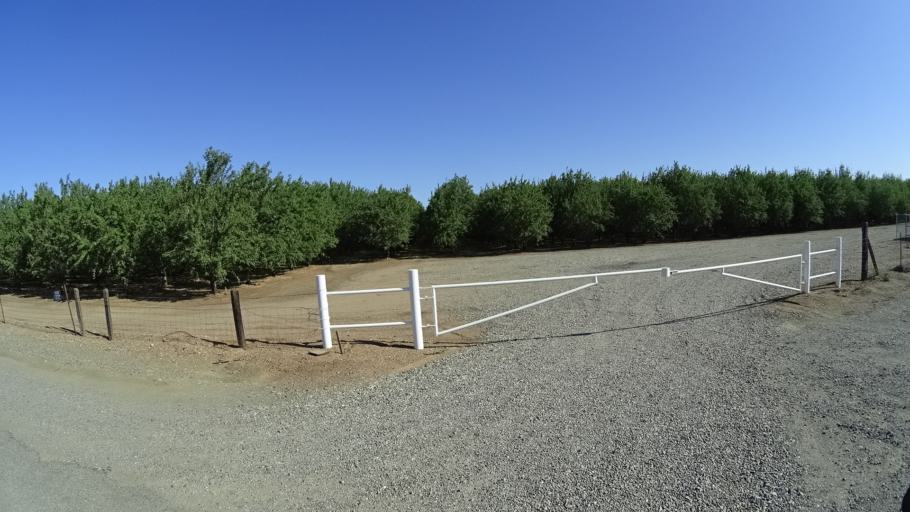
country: US
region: California
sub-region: Glenn County
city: Hamilton City
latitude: 39.6780
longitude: -122.0165
